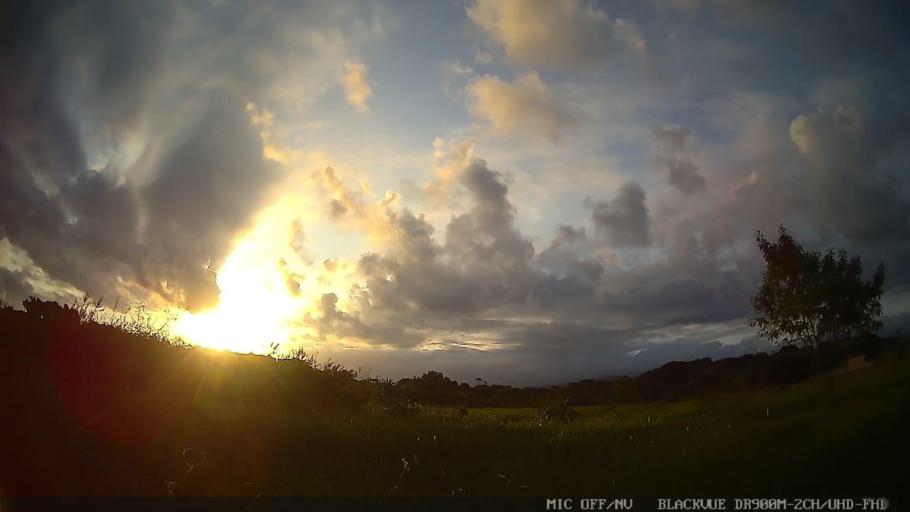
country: BR
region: Sao Paulo
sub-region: Itanhaem
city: Itanhaem
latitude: -24.1821
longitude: -46.8356
